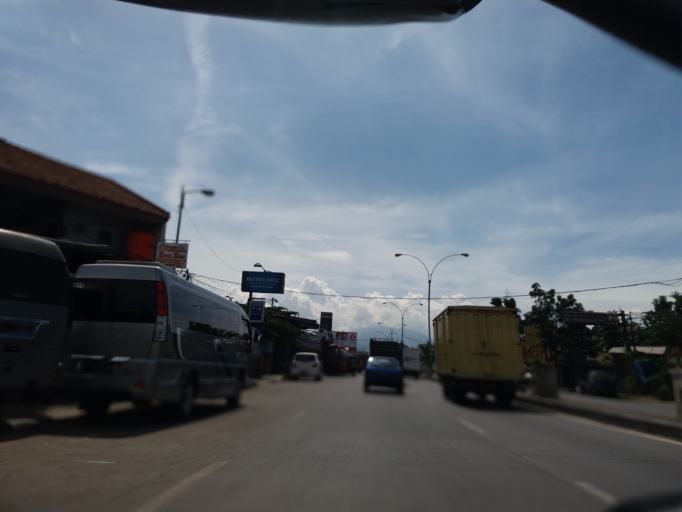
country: ID
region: West Java
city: Margahayukencana
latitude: -6.9289
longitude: 107.5757
